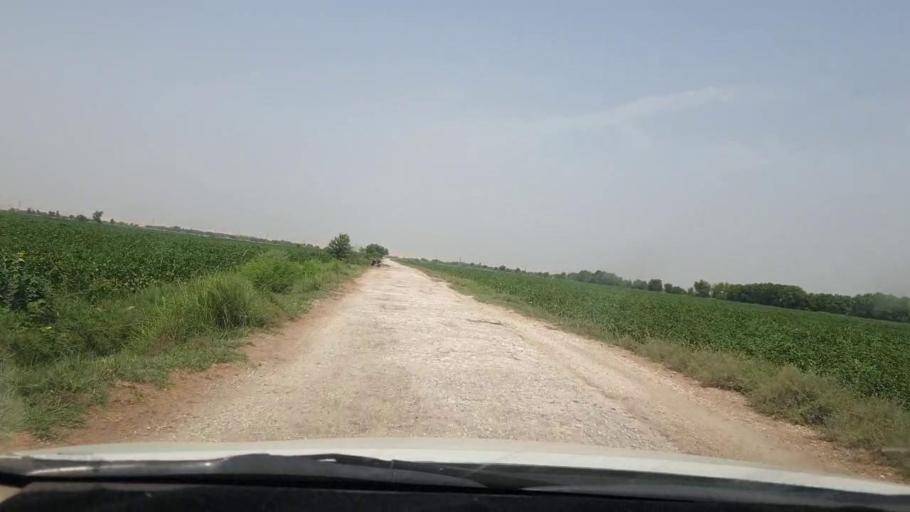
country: PK
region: Sindh
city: Rohri
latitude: 27.4978
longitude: 69.0177
